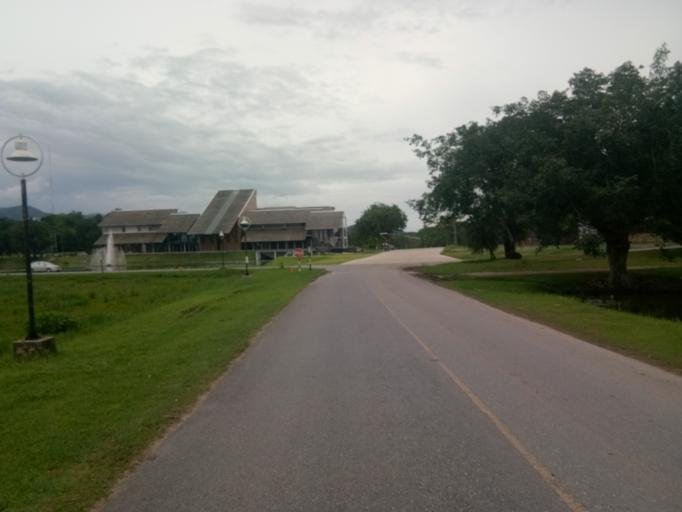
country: TH
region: Chiang Rai
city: Chiang Rai
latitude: 19.9824
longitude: 99.8486
